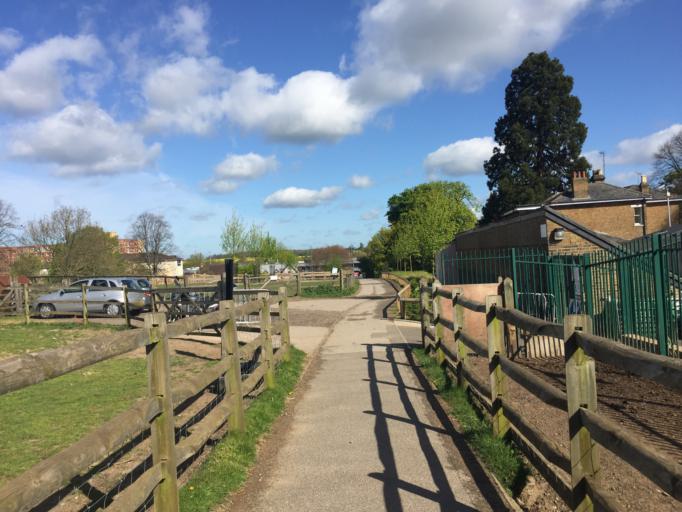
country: GB
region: England
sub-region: Essex
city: Harlow
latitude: 51.7788
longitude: 0.0992
